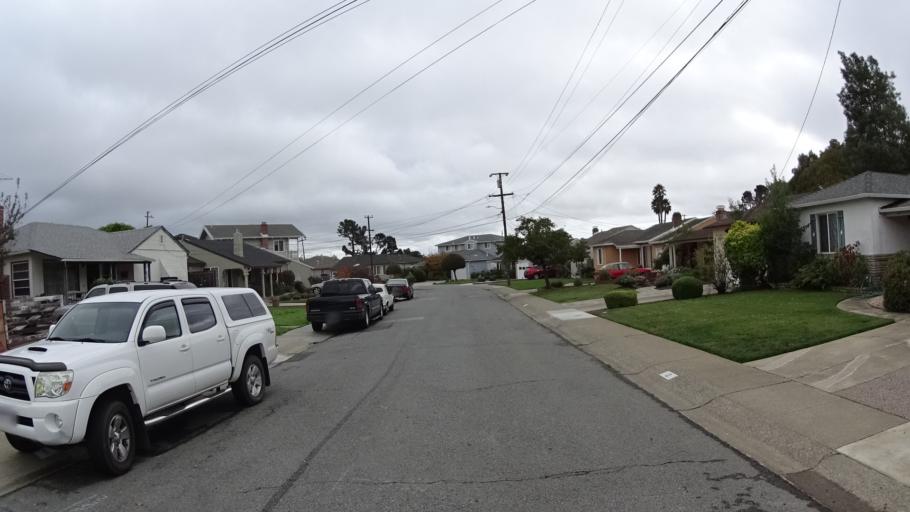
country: US
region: California
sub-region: San Mateo County
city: San Bruno
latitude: 37.6124
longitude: -122.4085
